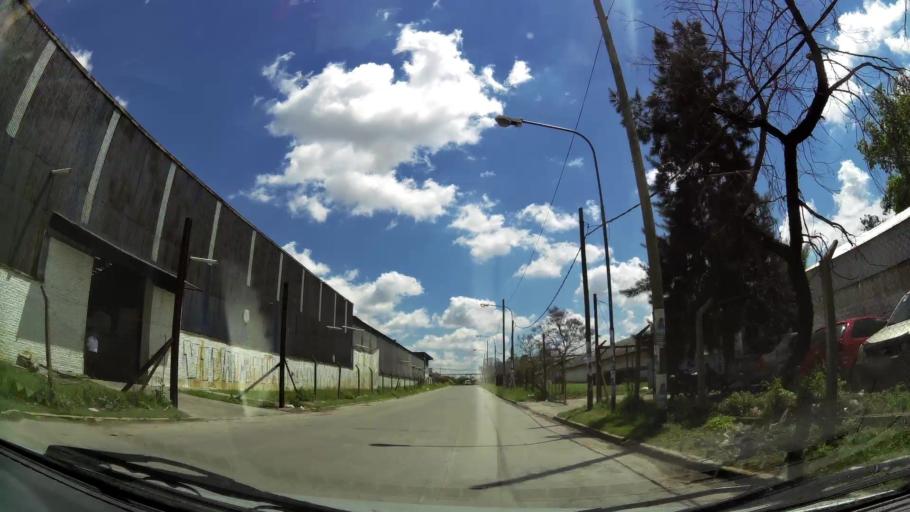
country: AR
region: Buenos Aires F.D.
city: Villa Lugano
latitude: -34.6839
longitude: -58.4398
